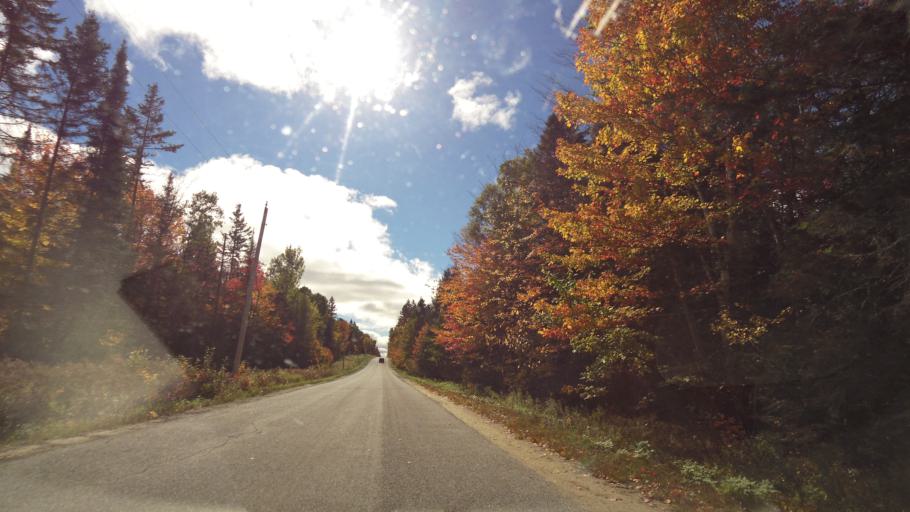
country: CA
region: Ontario
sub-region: Nipissing District
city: North Bay
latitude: 46.3611
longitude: -79.4872
